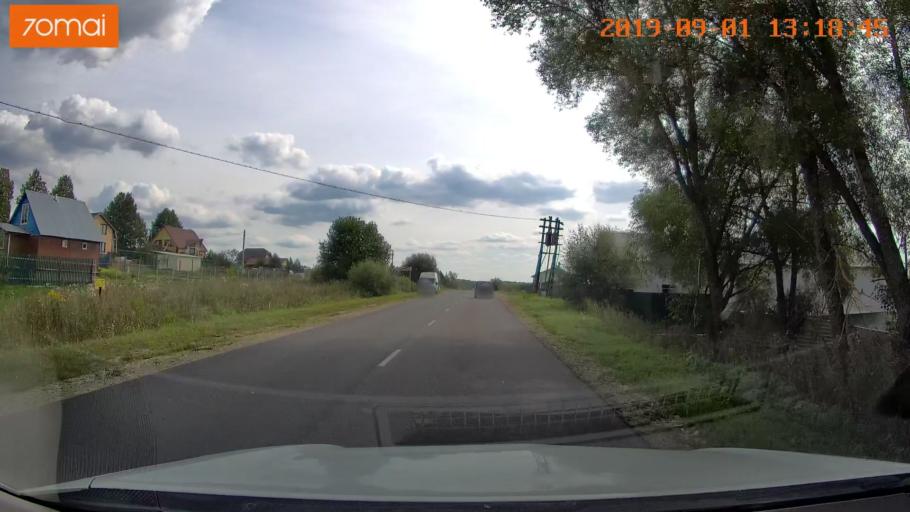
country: RU
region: Kaluga
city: Maloyaroslavets
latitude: 54.9233
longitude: 36.4764
